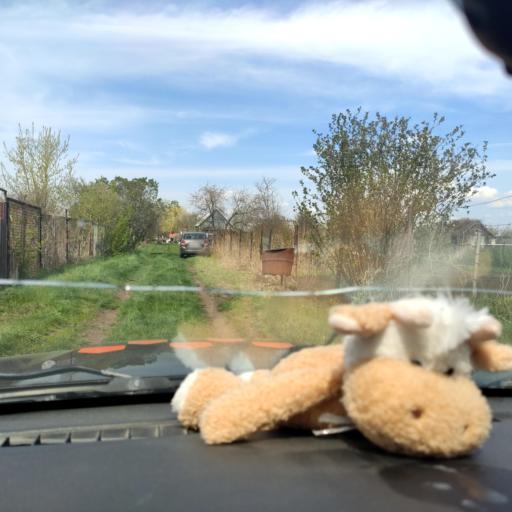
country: RU
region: Samara
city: Podstepki
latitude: 53.5116
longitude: 49.0855
